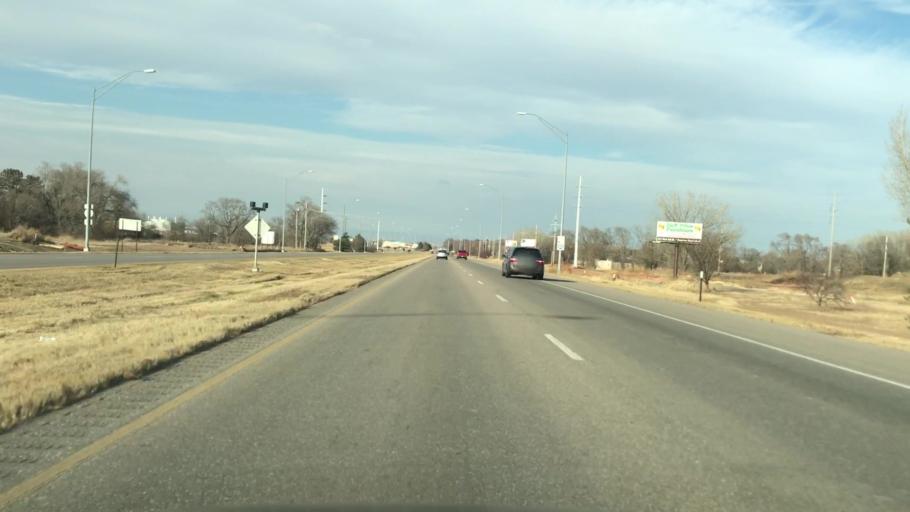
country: US
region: Nebraska
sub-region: Hall County
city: Grand Island
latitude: 40.8896
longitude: -98.3783
